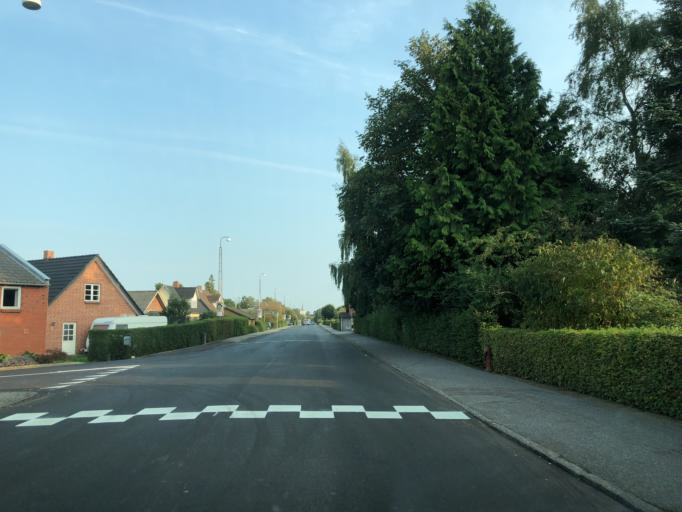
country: DK
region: South Denmark
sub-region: Vejle Kommune
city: Jelling
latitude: 55.7090
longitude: 9.3753
